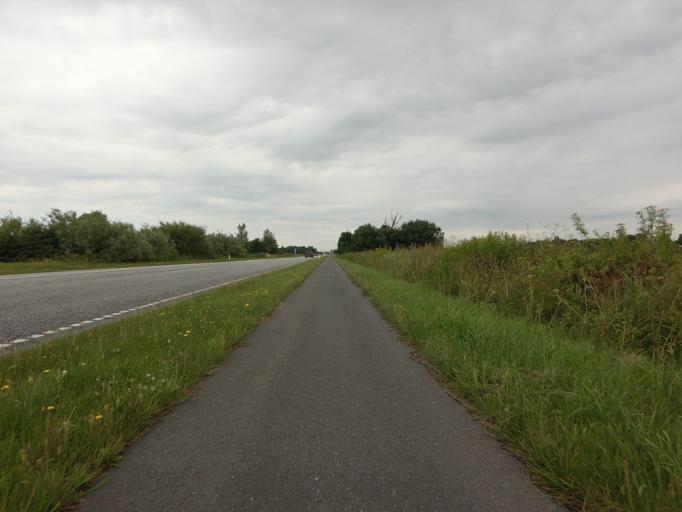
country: DK
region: North Denmark
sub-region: Alborg Kommune
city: Aalborg
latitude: 57.0792
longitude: 9.8908
